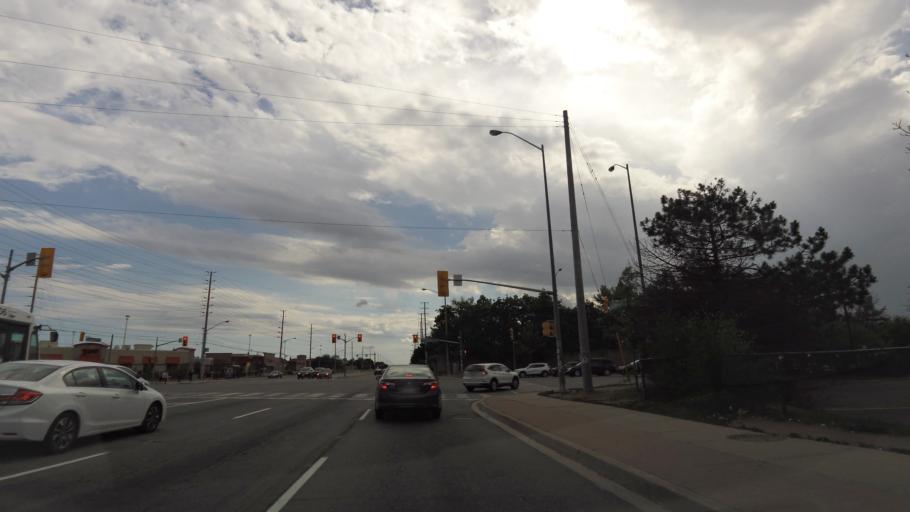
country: CA
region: Ontario
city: Brampton
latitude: 43.6568
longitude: -79.7435
